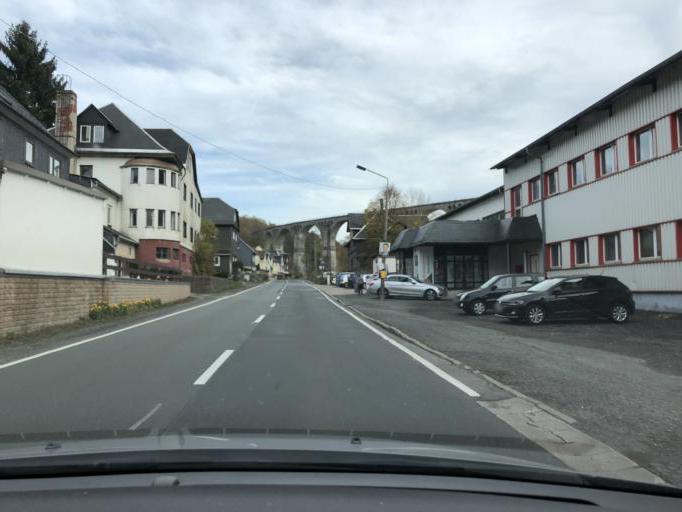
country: DE
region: Thuringia
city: Lichte
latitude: 50.5254
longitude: 11.1989
